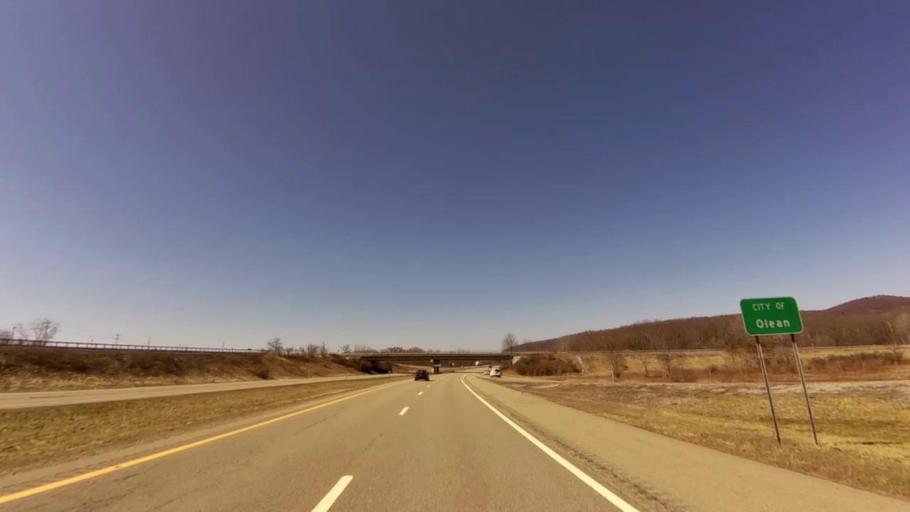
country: US
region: New York
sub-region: Cattaraugus County
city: Franklinville
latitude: 42.3105
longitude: -78.4602
